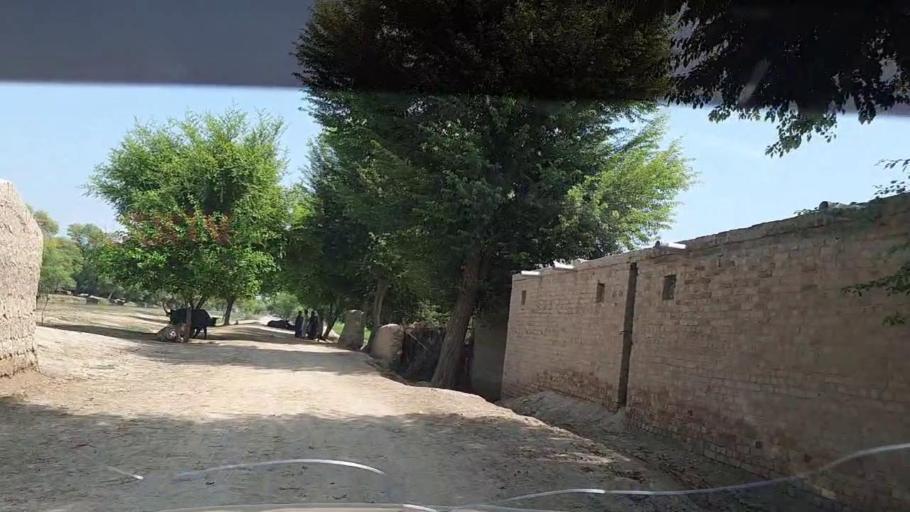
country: PK
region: Sindh
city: Tangwani
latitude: 28.2326
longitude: 68.9472
